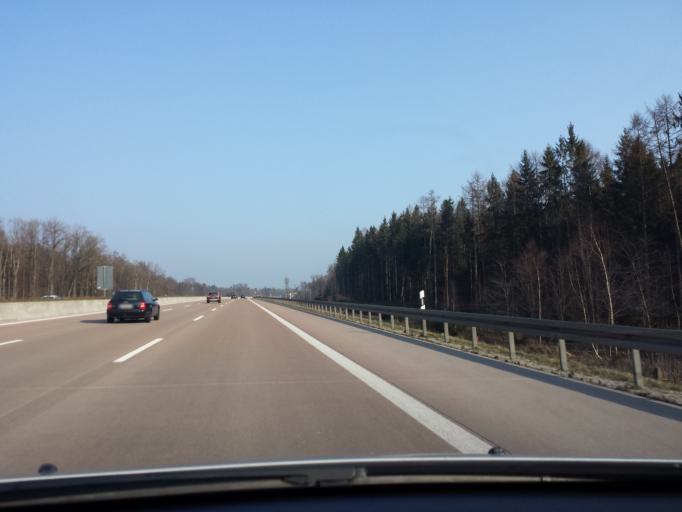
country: DE
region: Bavaria
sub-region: Swabia
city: Landensberg
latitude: 48.4092
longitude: 10.4994
